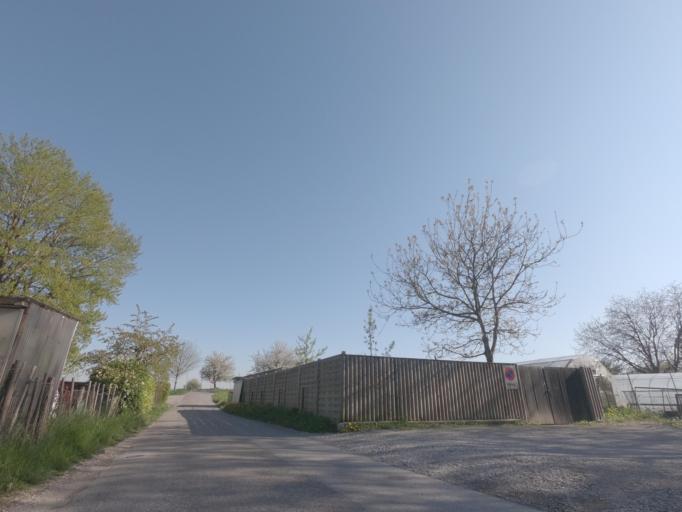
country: CH
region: Bern
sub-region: Biel/Bienne District
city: Lengnau
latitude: 47.1834
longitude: 7.3787
